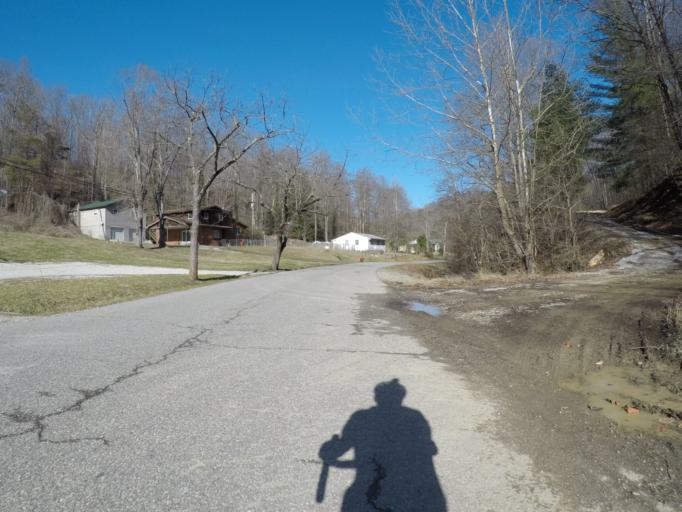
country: US
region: Kentucky
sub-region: Boyd County
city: Catlettsburg
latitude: 38.4176
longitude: -82.6406
